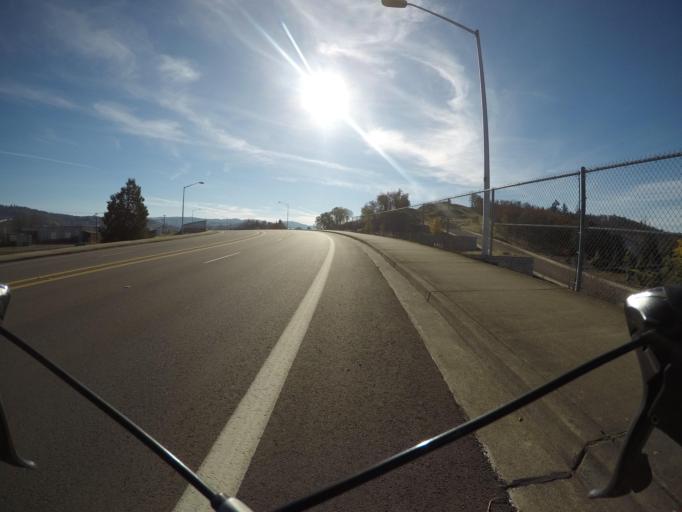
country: US
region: Oregon
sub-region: Douglas County
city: Roseburg
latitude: 43.2377
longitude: -123.3615
